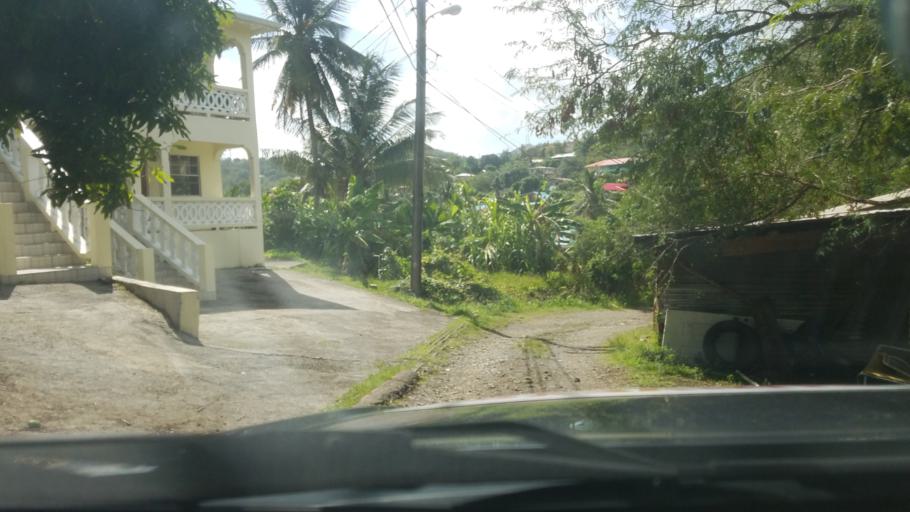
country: LC
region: Gros-Islet
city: Gros Islet
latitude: 14.0606
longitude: -60.9458
